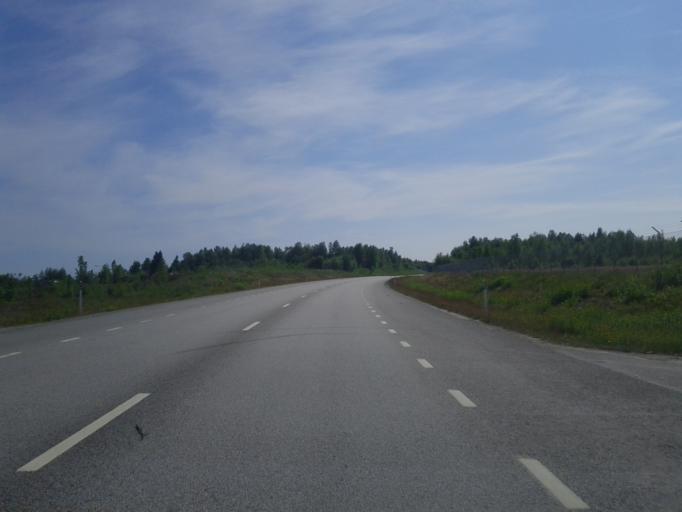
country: SE
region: Vaesterbotten
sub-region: Umea Kommun
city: Umea
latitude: 63.7814
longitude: 20.3037
